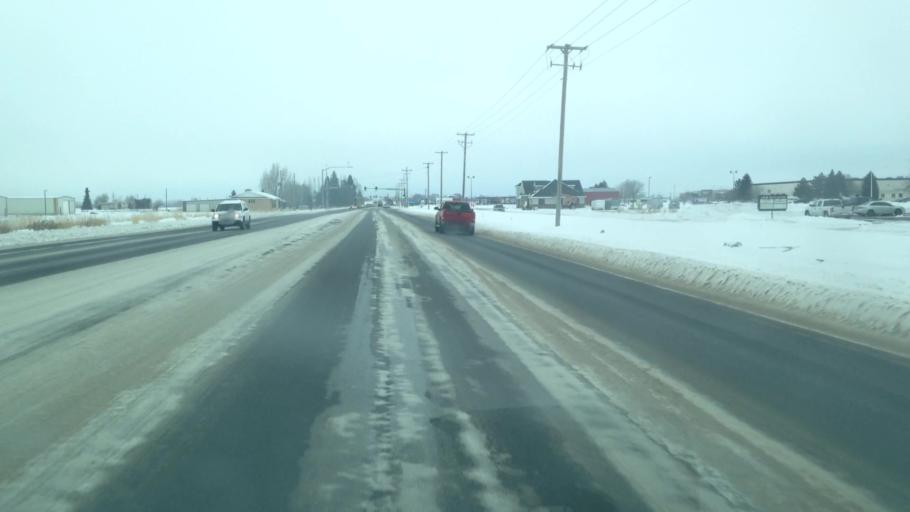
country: US
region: Idaho
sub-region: Madison County
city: Rexburg
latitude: 43.8492
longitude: -111.7779
